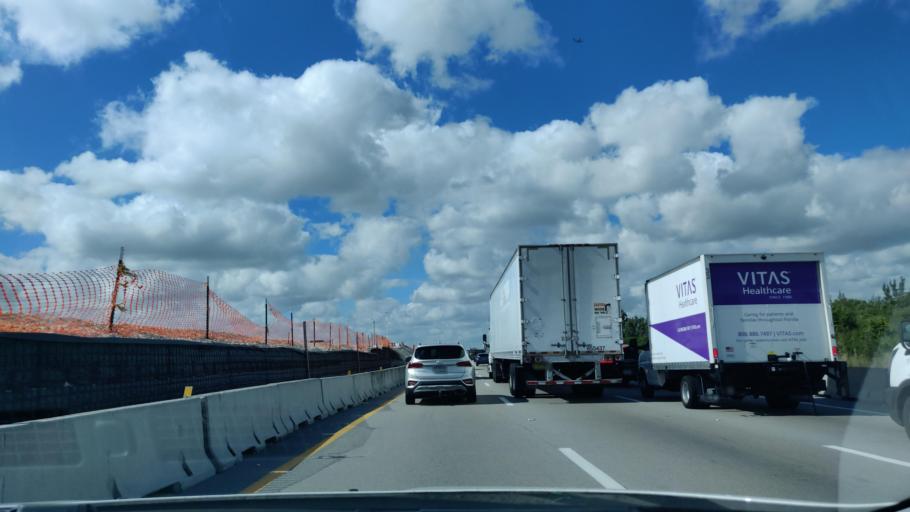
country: US
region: Florida
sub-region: Miami-Dade County
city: Palm Springs North
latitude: 25.9329
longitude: -80.3717
